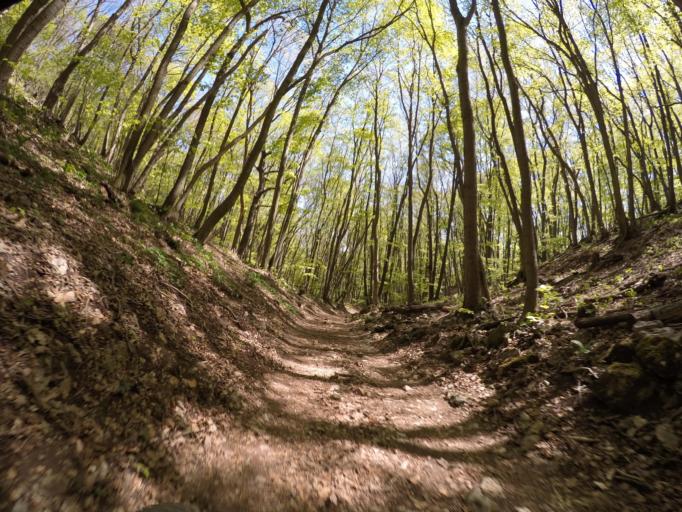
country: AT
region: Lower Austria
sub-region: Politischer Bezirk Modling
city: Gumpoldskirchen
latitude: 48.0479
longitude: 16.2598
